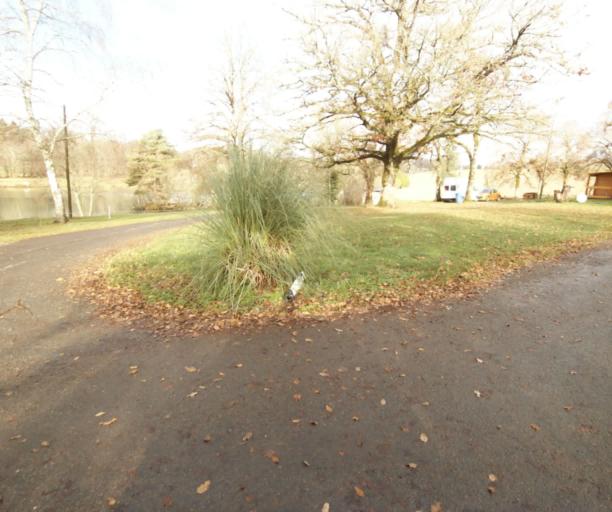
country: FR
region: Limousin
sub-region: Departement de la Correze
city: Sainte-Fereole
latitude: 45.2733
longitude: 1.5959
